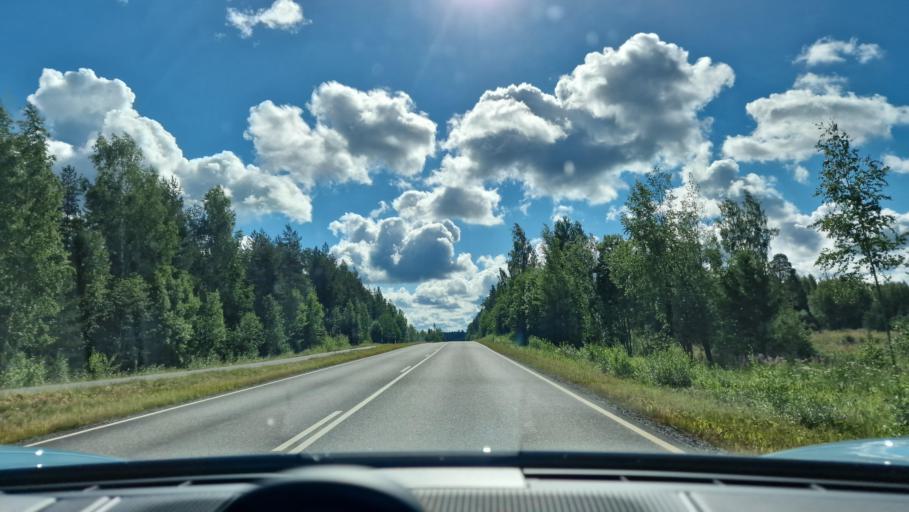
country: FI
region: Pirkanmaa
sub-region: Tampere
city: Paelkaene
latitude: 61.2530
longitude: 24.1803
